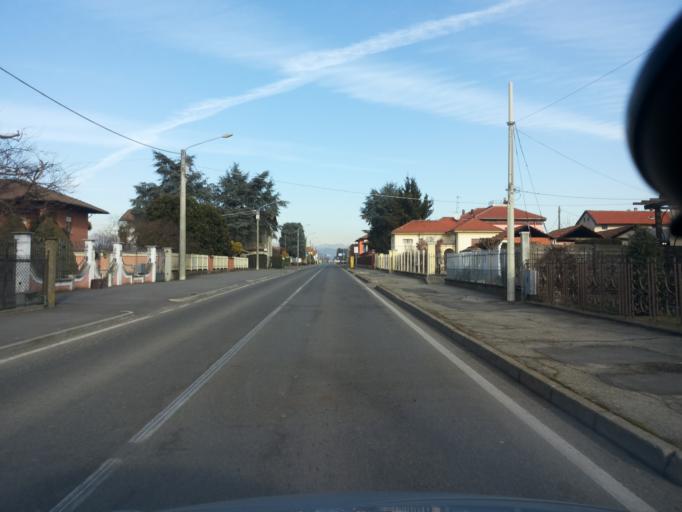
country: IT
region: Piedmont
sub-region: Provincia di Vercelli
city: Arborio
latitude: 45.4999
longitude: 8.3895
